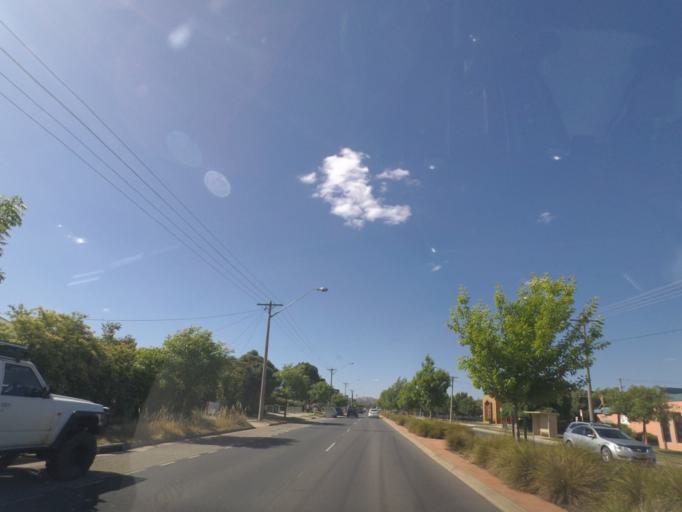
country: AU
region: New South Wales
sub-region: Albury Municipality
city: North Albury
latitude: -36.0592
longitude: 146.9323
